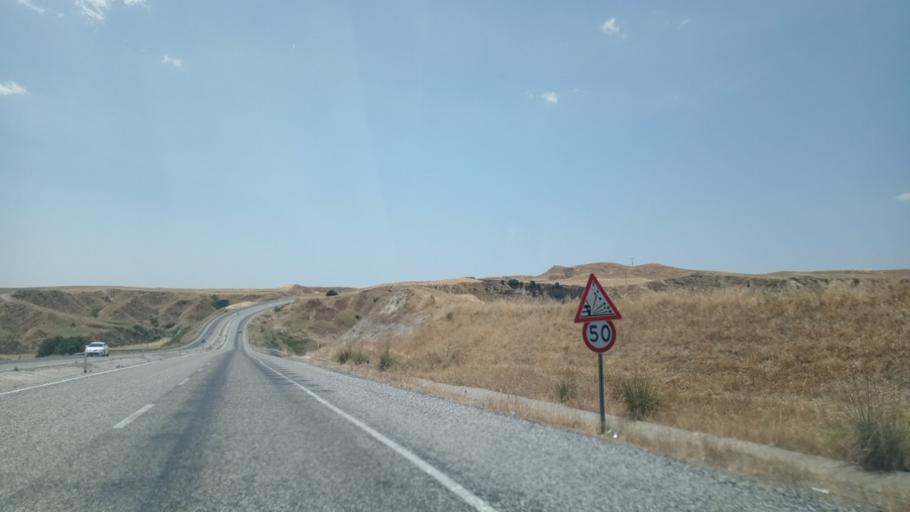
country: TR
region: Batman
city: Bekirhan
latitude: 38.1411
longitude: 41.2776
